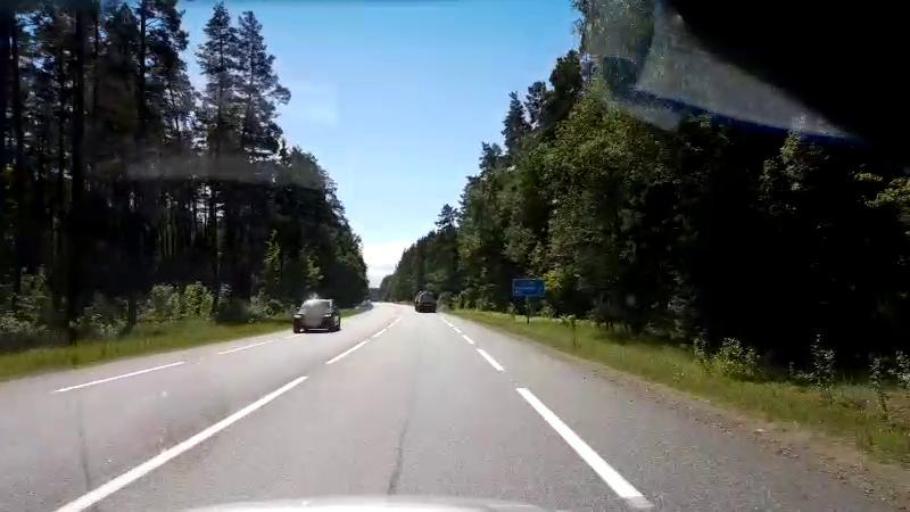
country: LV
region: Saulkrastu
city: Saulkrasti
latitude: 57.3961
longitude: 24.4281
